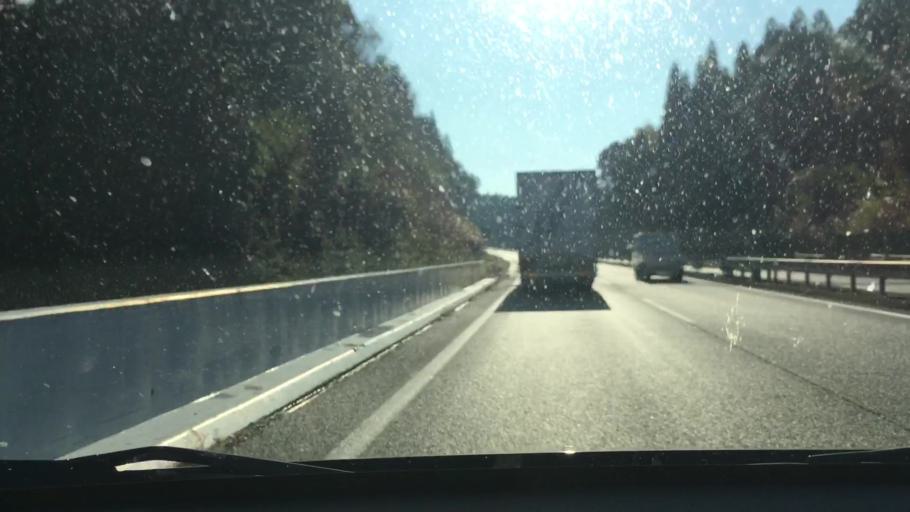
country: JP
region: Kagoshima
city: Okuchi-shinohara
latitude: 31.9391
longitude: 130.7111
